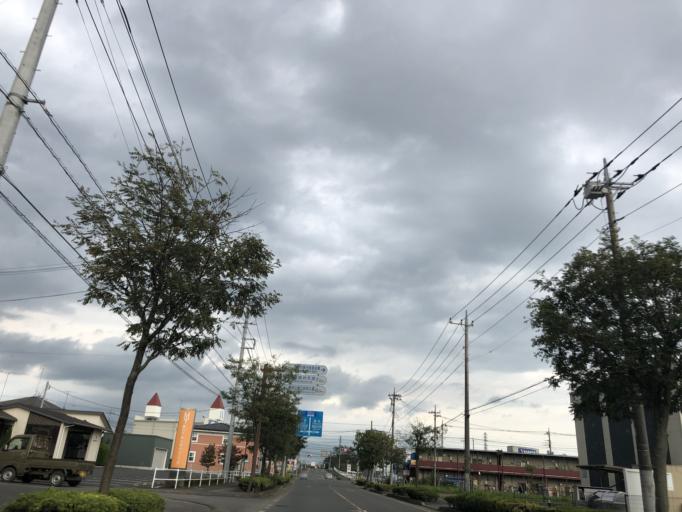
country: JP
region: Tochigi
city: Sano
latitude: 36.3226
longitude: 139.5638
